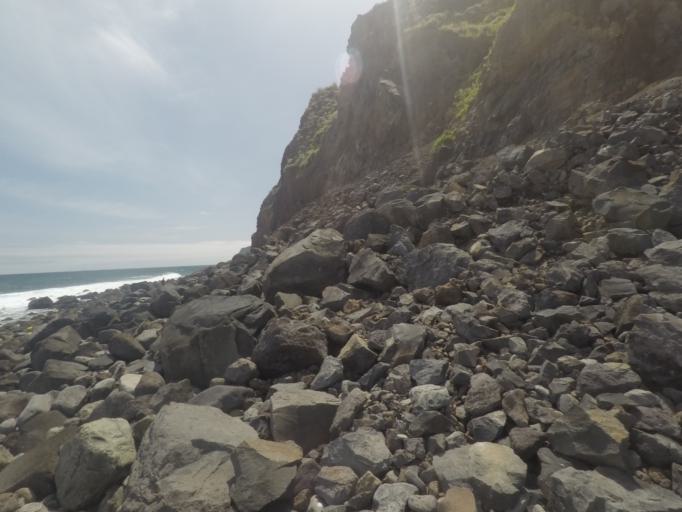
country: PT
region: Madeira
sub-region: Sao Vicente
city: Sao Vicente
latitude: 32.8302
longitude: -16.9898
